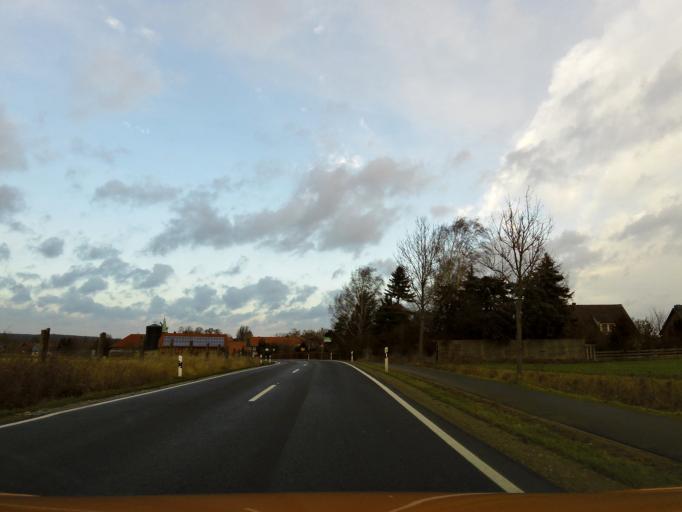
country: DE
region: Lower Saxony
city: Gross Twulpstedt
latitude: 52.3691
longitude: 10.9207
